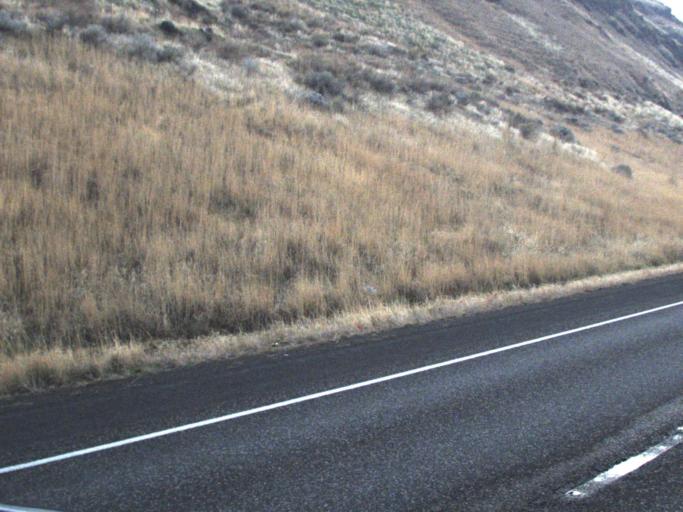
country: US
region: Washington
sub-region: Asotin County
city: Clarkston Heights-Vineland
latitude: 46.4255
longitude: -117.1589
